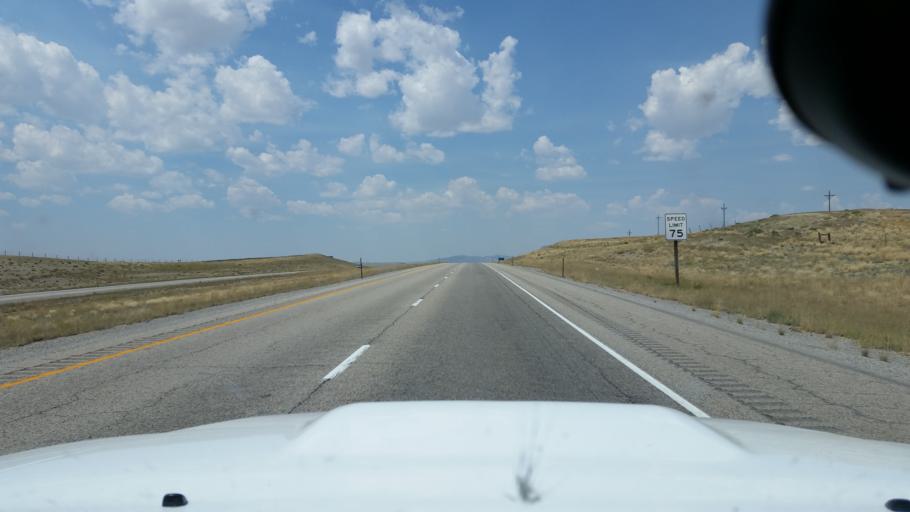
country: US
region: Wyoming
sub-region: Carbon County
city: Rawlins
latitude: 41.7563
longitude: -106.9718
